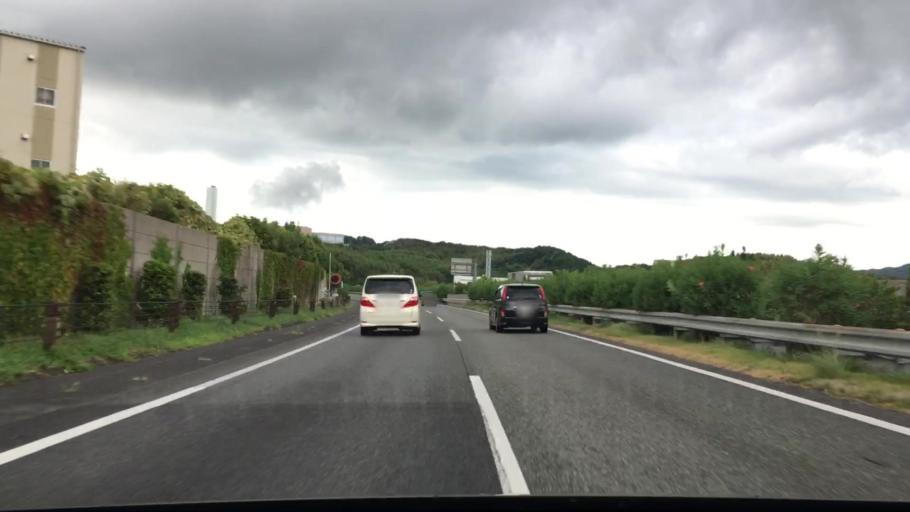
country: JP
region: Fukuoka
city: Sasaguri
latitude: 33.6355
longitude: 130.4907
